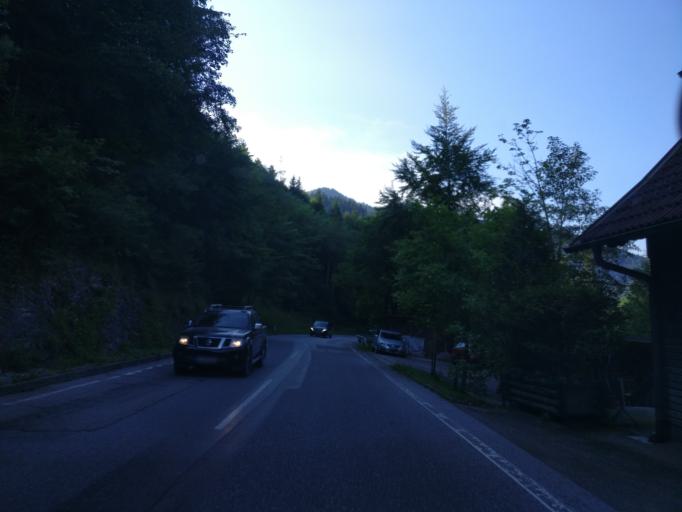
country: AT
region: Lower Austria
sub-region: Politischer Bezirk Scheibbs
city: Gostling an der Ybbs
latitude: 47.7695
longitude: 14.9068
